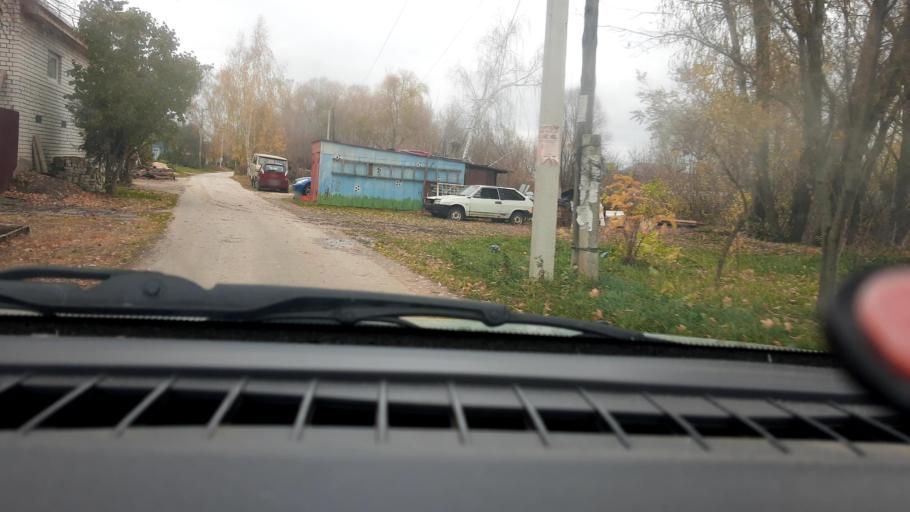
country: RU
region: Nizjnij Novgorod
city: Afonino
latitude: 56.2714
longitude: 44.1049
